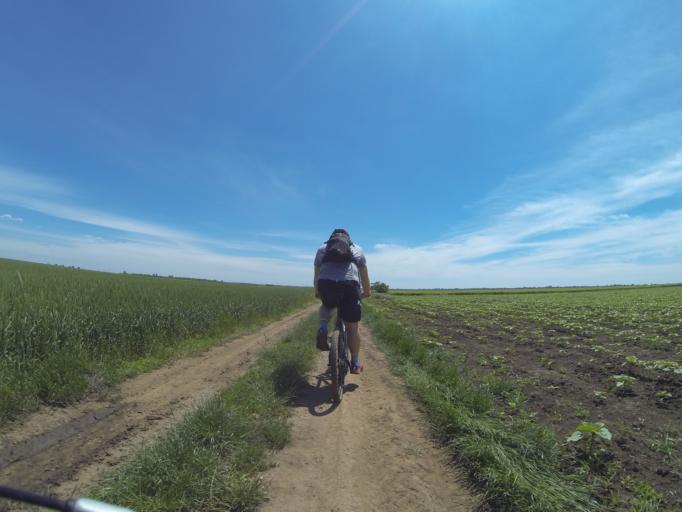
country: RO
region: Dolj
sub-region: Comuna Leu
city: Zanoaga
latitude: 44.1798
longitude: 24.0795
